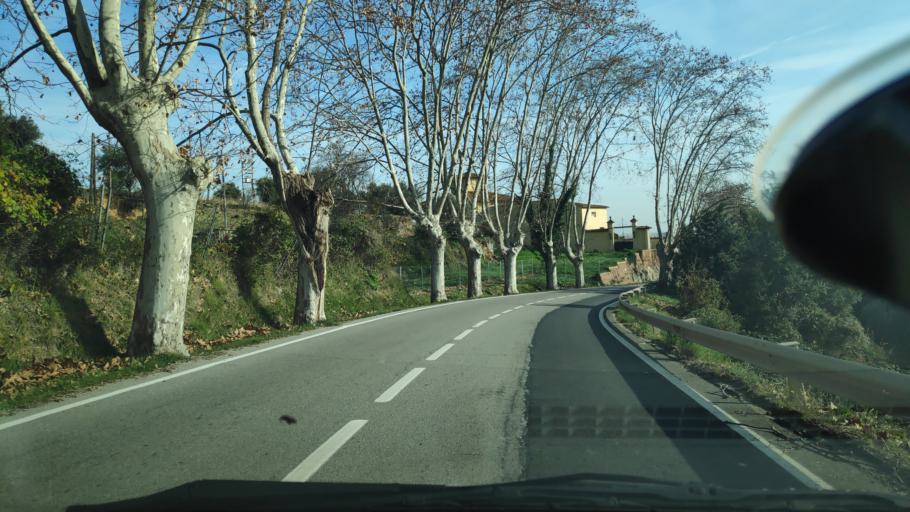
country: ES
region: Catalonia
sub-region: Provincia de Barcelona
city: Castellar del Valles
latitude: 41.6092
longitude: 2.0739
